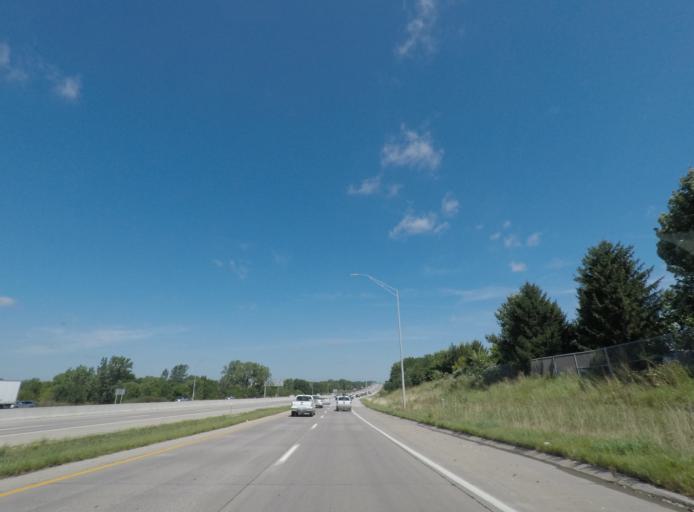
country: US
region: Iowa
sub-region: Polk County
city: Clive
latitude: 41.5621
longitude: -93.7763
